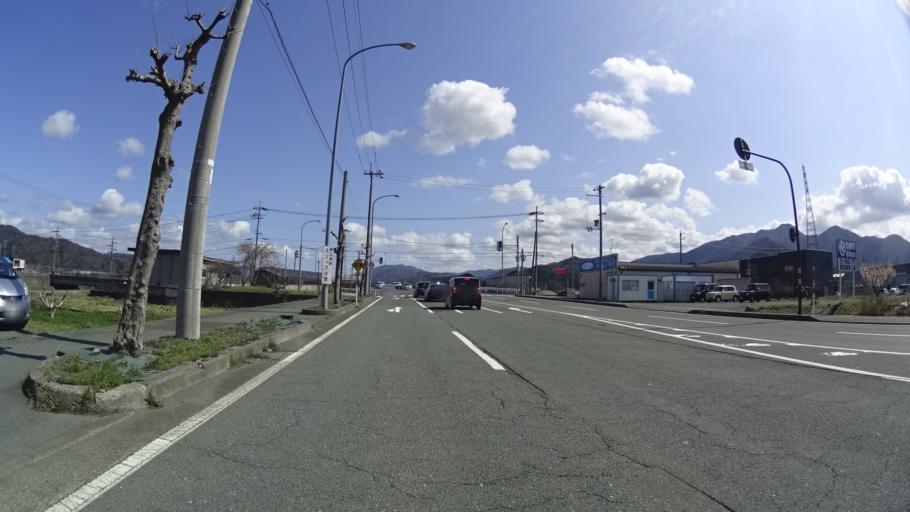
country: JP
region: Fukui
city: Obama
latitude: 35.4936
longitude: 135.7601
